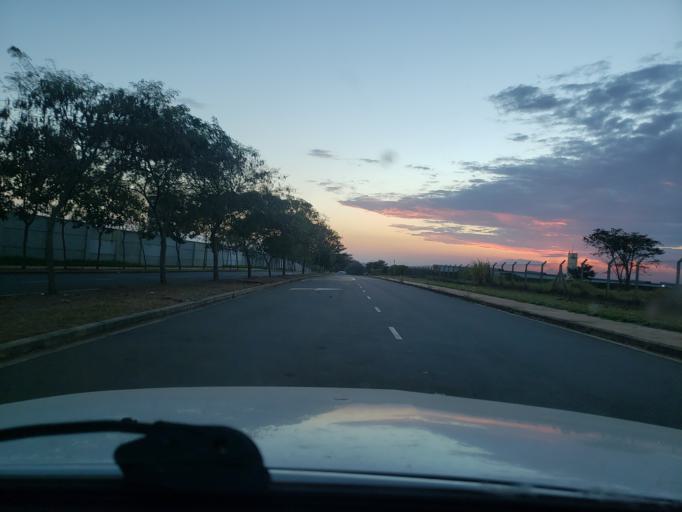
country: BR
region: Sao Paulo
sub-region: Mogi-Mirim
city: Mogi Mirim
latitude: -22.4892
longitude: -46.9767
